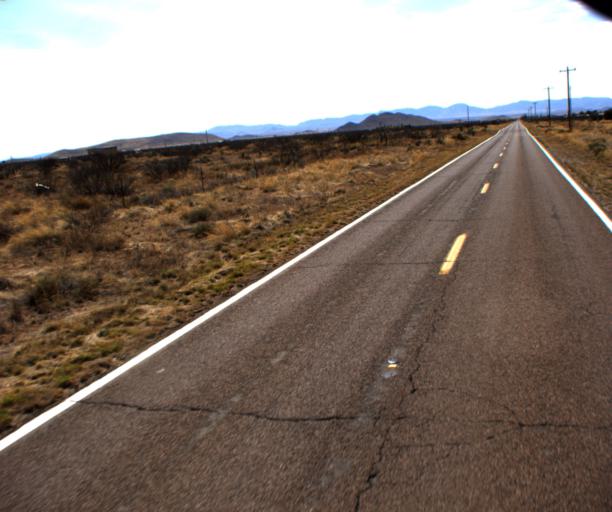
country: US
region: Arizona
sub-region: Cochise County
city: Willcox
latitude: 31.8762
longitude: -109.5987
